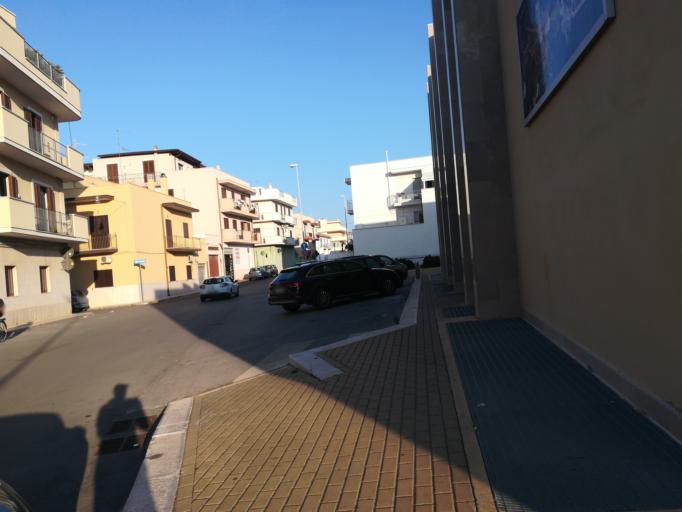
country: IT
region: Apulia
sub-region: Provincia di Bari
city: Polignano a Mare
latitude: 40.9941
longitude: 17.2257
